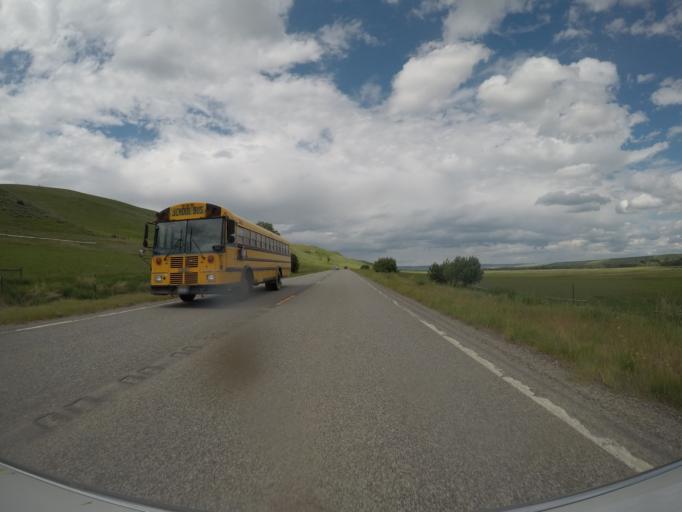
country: US
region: Montana
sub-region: Sweet Grass County
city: Big Timber
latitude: 45.7801
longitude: -109.9853
